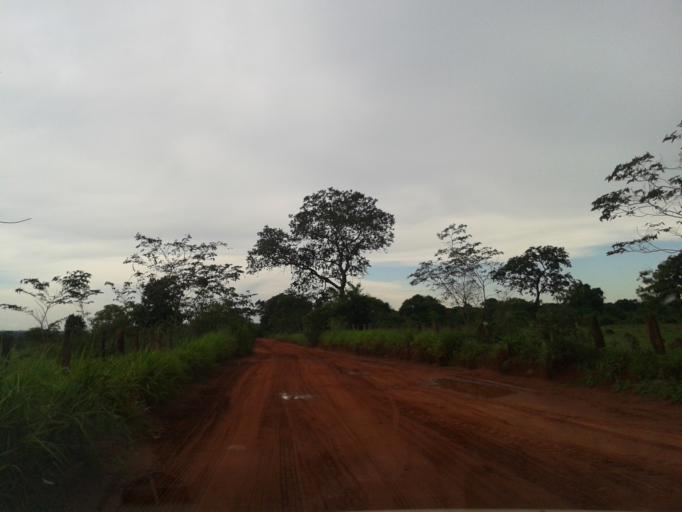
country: BR
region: Minas Gerais
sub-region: Santa Vitoria
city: Santa Vitoria
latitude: -19.1355
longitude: -50.5558
